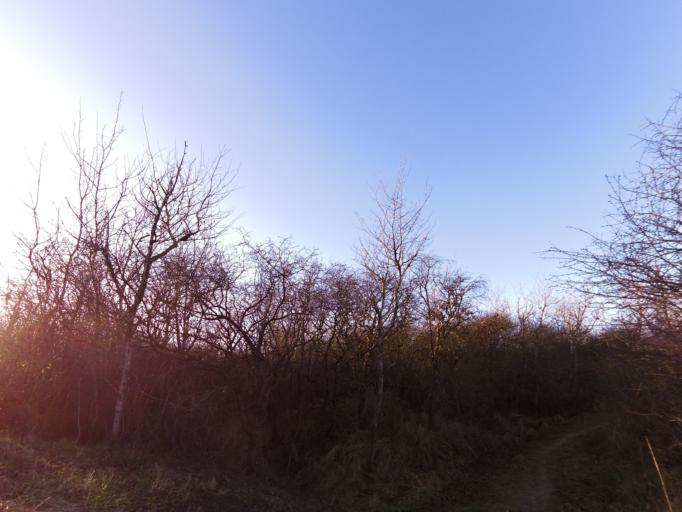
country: NL
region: South Holland
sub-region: Gemeente Goeree-Overflakkee
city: Goedereede
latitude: 51.8841
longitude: 4.0365
